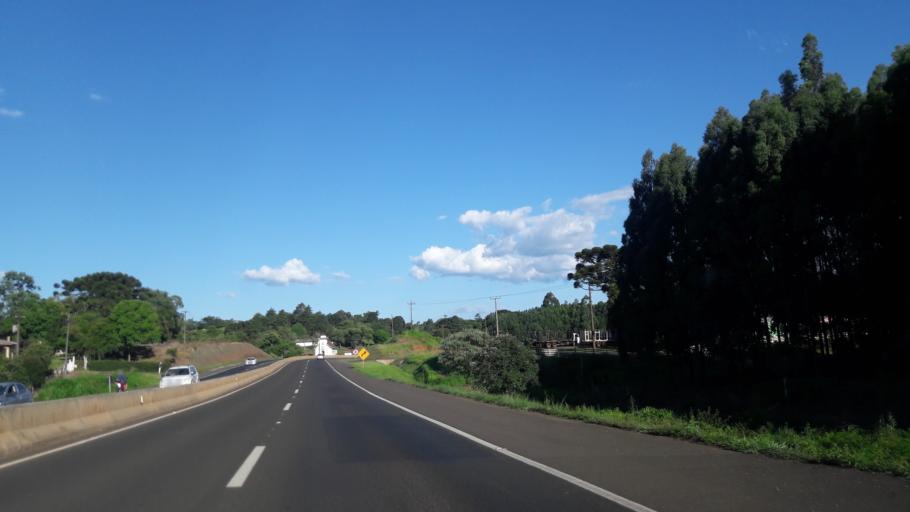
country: BR
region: Parana
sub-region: Guarapuava
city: Guarapuava
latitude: -25.3443
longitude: -51.3956
